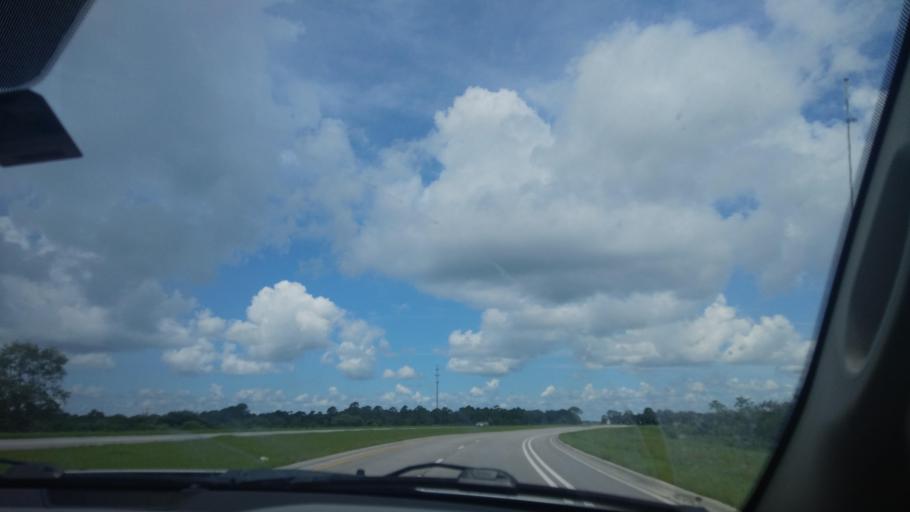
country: US
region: Florida
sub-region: Brevard County
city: Grant-Valkaria
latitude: 27.8938
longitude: -80.6069
